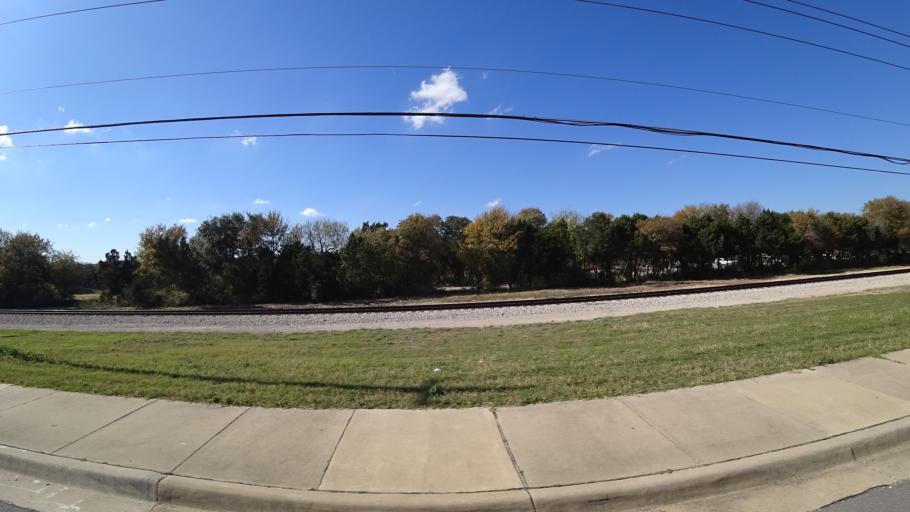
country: US
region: Texas
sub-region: Travis County
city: Wells Branch
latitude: 30.4249
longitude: -97.7032
